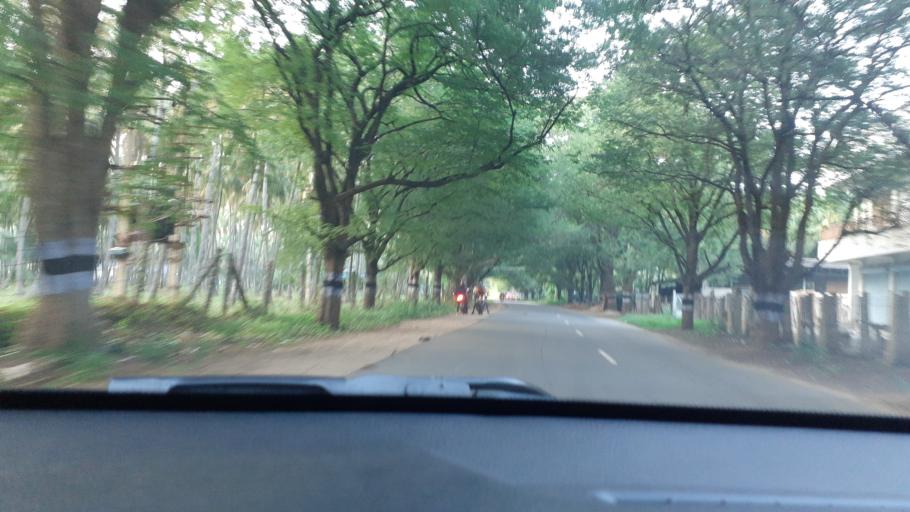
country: IN
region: Tamil Nadu
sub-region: Dindigul
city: Palani
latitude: 10.4207
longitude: 77.5347
